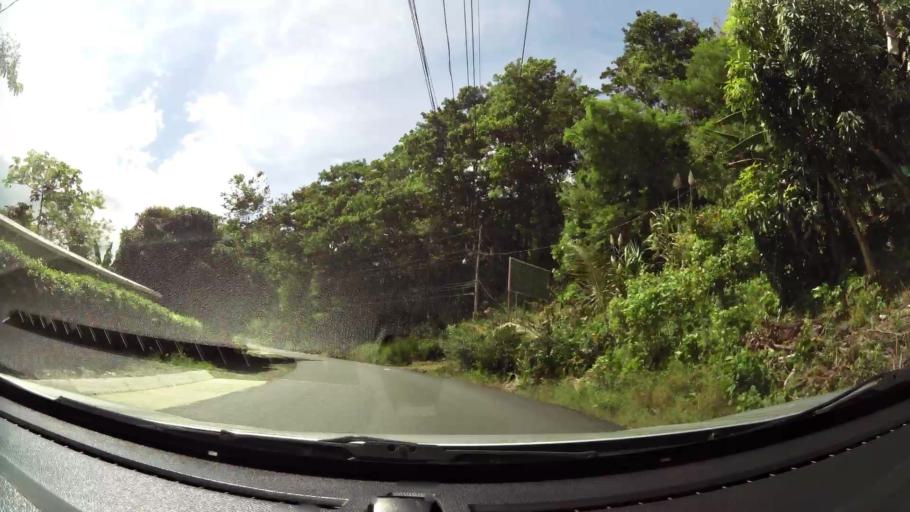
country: CR
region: San Jose
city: San Isidro
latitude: 9.3315
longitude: -83.7393
